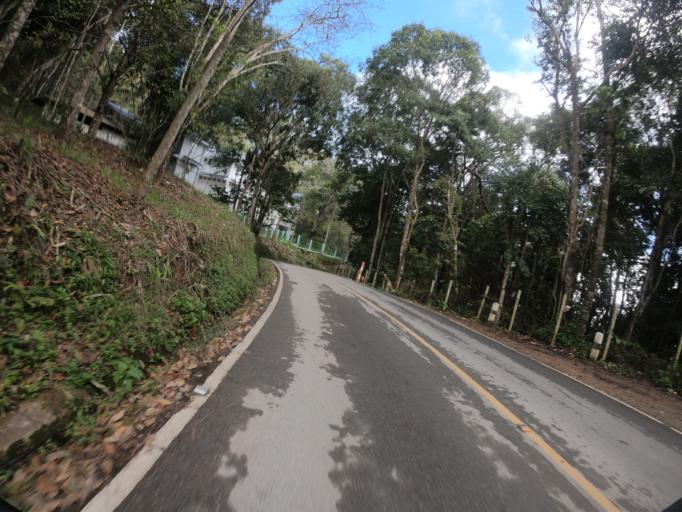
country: TH
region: Chiang Mai
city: Chiang Mai
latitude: 18.8060
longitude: 98.8960
